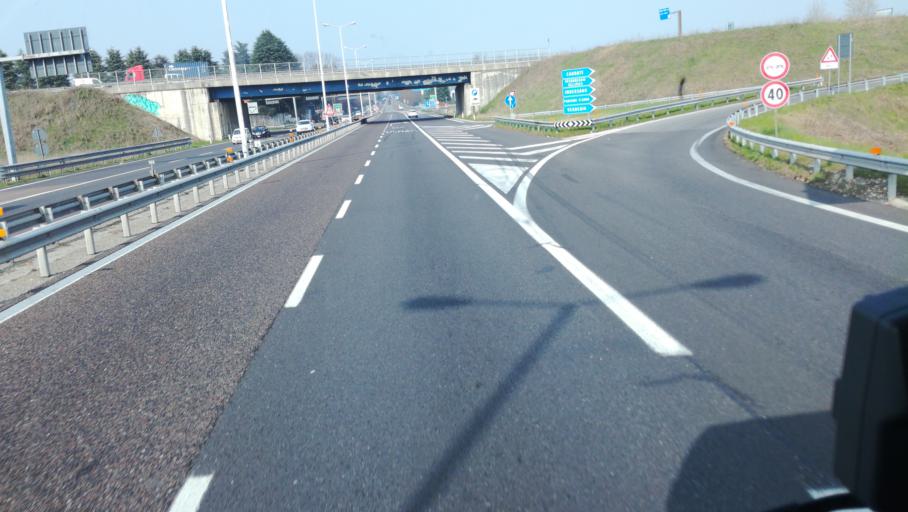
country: IT
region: Lombardy
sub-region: Provincia di Monza e Brianza
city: Usmate-Velate
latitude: 45.6411
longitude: 9.3652
